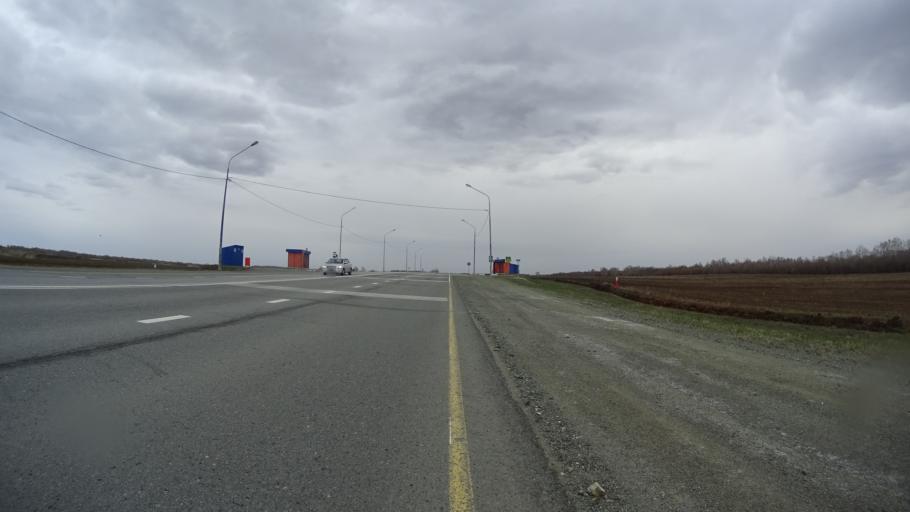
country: RU
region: Chelyabinsk
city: Krasnogorskiy
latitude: 54.6725
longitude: 61.2497
